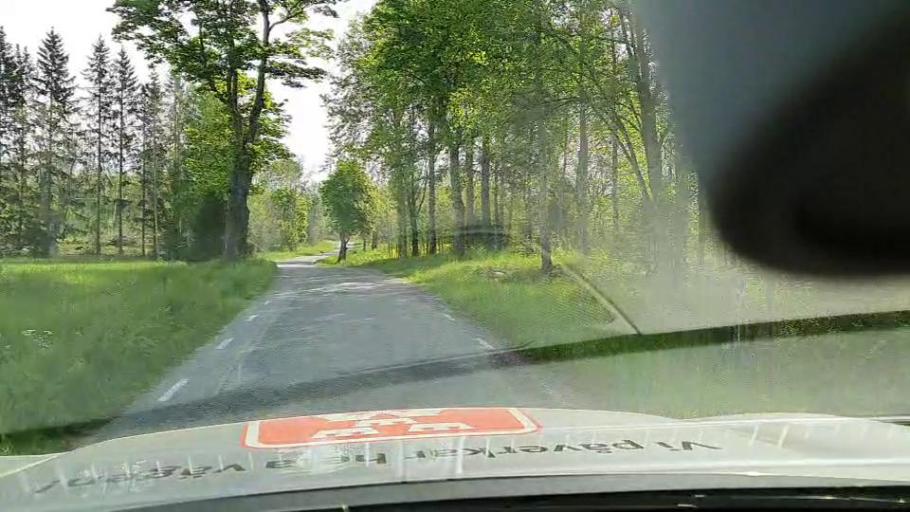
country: SE
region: Soedermanland
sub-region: Eskilstuna Kommun
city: Arla
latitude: 59.2584
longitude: 16.6676
